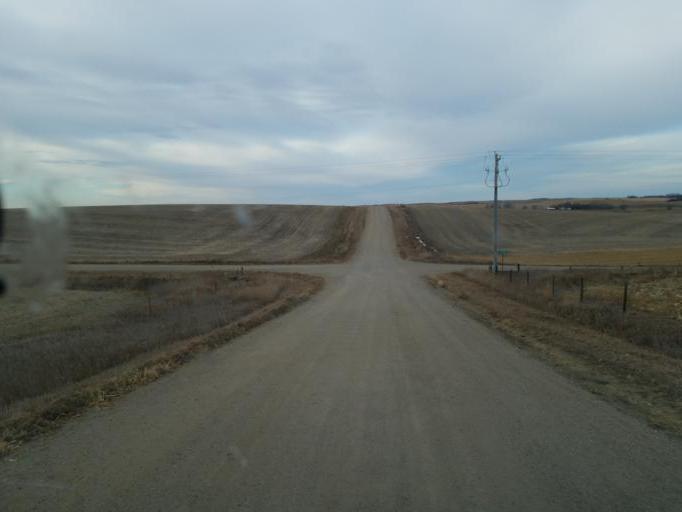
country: US
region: Nebraska
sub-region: Knox County
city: Bloomfield
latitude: 42.5688
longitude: -97.6613
